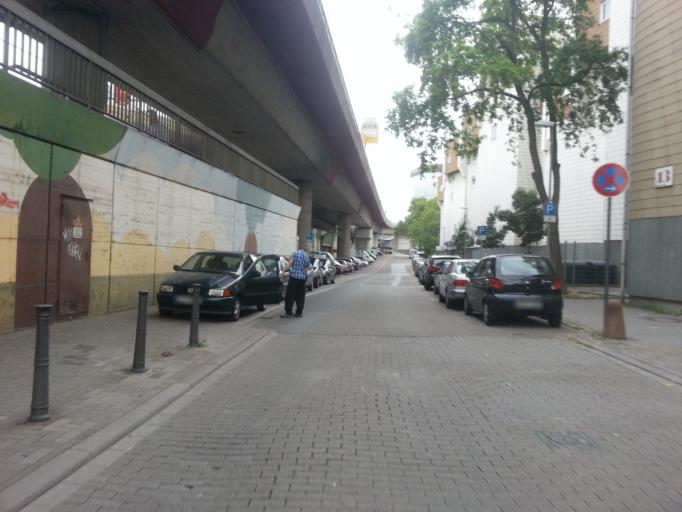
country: DE
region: Rheinland-Pfalz
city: Ludwigshafen am Rhein
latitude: 49.4888
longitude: 8.4408
